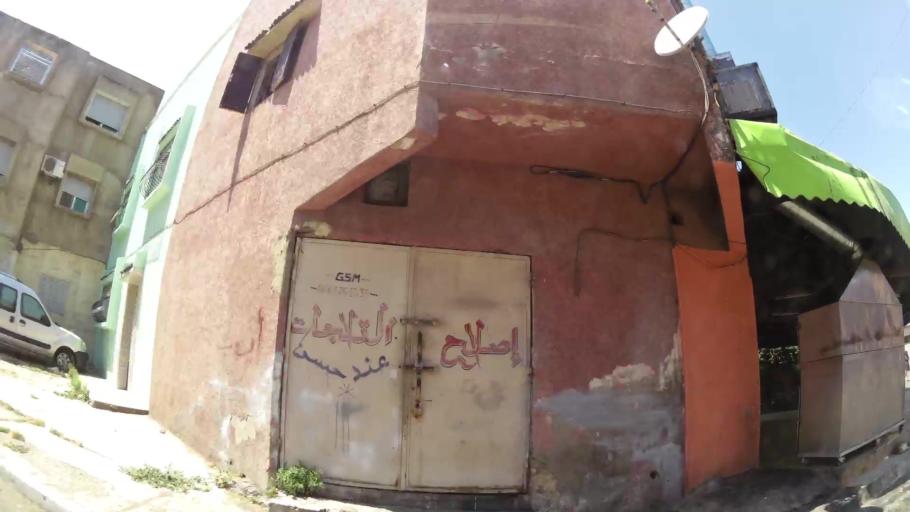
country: MA
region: Gharb-Chrarda-Beni Hssen
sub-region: Kenitra Province
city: Kenitra
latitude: 34.2587
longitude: -6.5544
